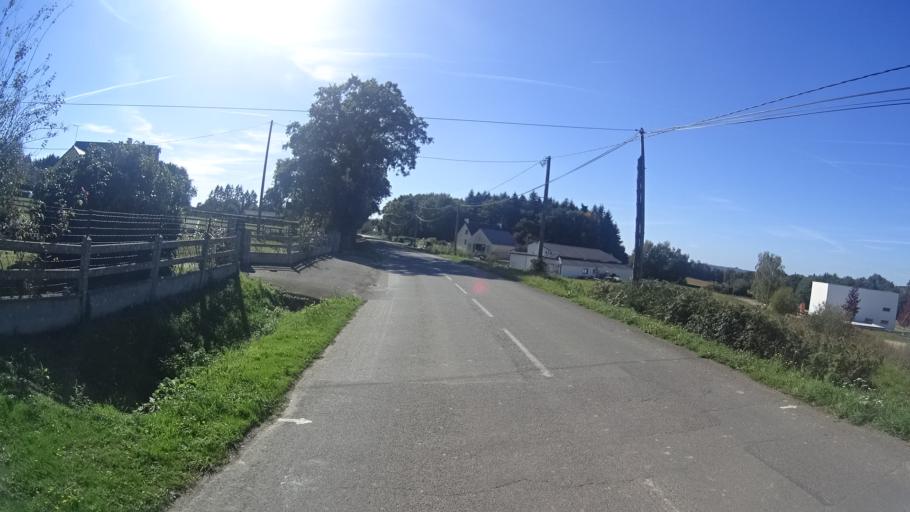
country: FR
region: Brittany
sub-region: Departement du Morbihan
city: Peillac
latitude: 47.7462
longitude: -2.2096
